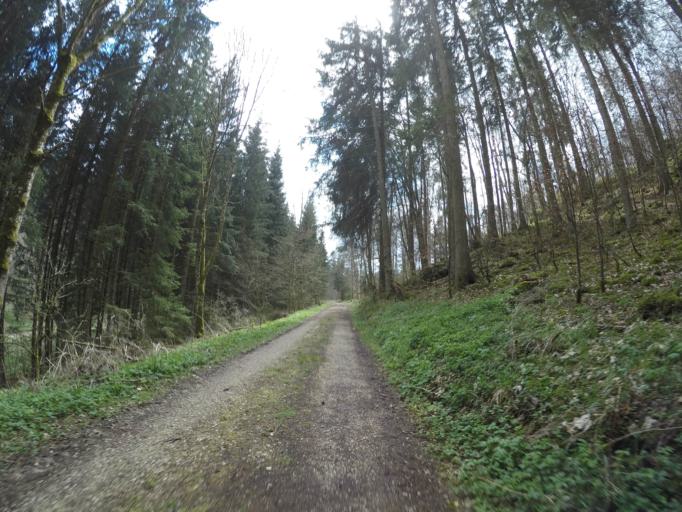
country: DE
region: Baden-Wuerttemberg
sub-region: Tuebingen Region
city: Berghulen
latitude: 48.4913
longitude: 9.7982
